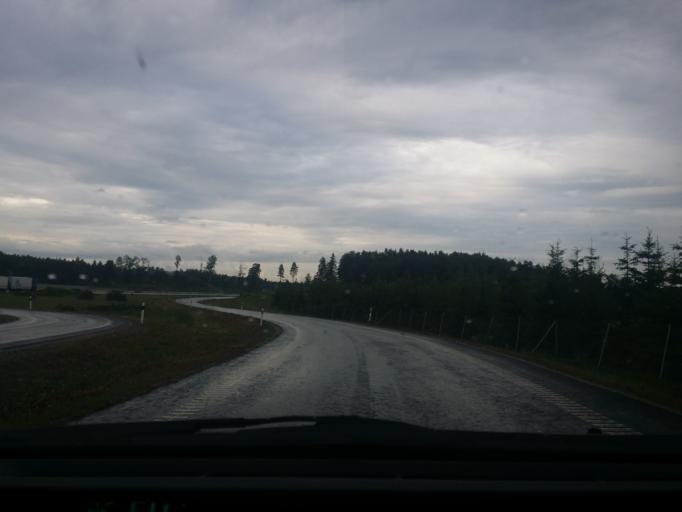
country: SE
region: Vaestmanland
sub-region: Arboga Kommun
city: Arboga
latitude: 59.4131
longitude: 15.7725
